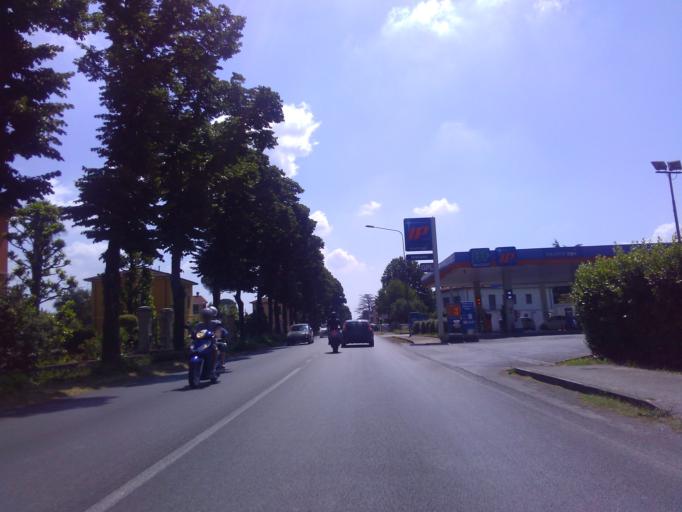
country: IT
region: Tuscany
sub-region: Provincia di Lucca
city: Lucca
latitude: 43.8487
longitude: 10.4659
